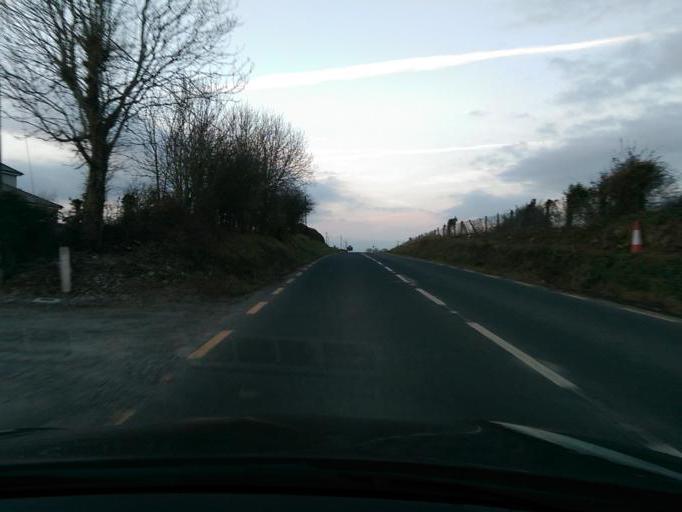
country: IE
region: Connaught
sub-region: County Galway
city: Portumna
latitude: 53.0151
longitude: -8.1252
